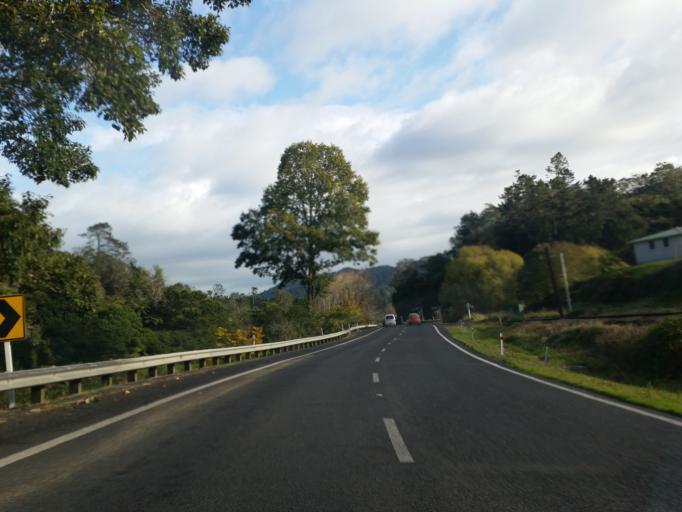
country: NZ
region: Waikato
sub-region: Hauraki District
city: Waihi
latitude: -37.4175
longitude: 175.7846
